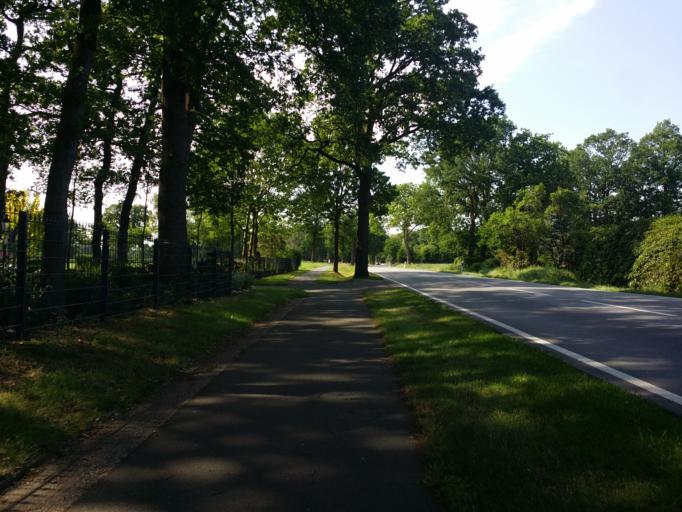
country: DE
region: Lower Saxony
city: Wiefelstede
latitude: 53.2770
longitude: 8.1098
